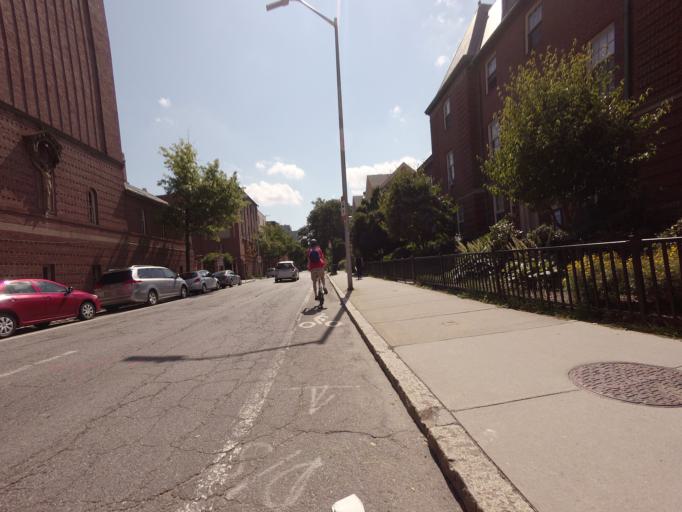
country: US
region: Massachusetts
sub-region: Middlesex County
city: Cambridge
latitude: 42.3710
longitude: -71.1160
